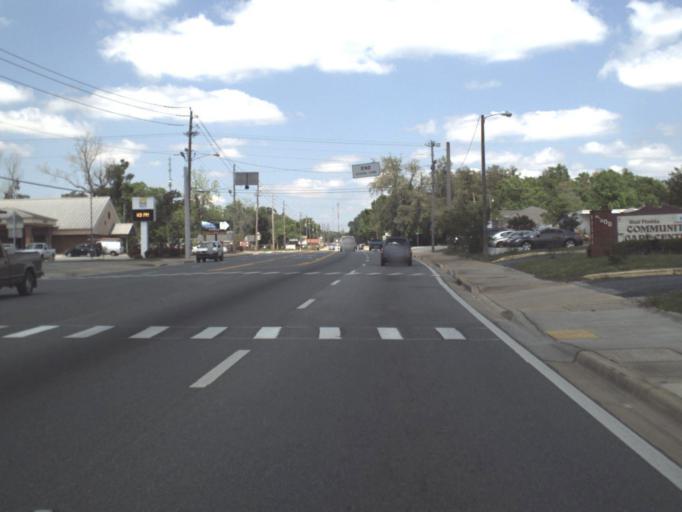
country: US
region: Florida
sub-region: Santa Rosa County
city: Milton
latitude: 30.6341
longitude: -87.0431
